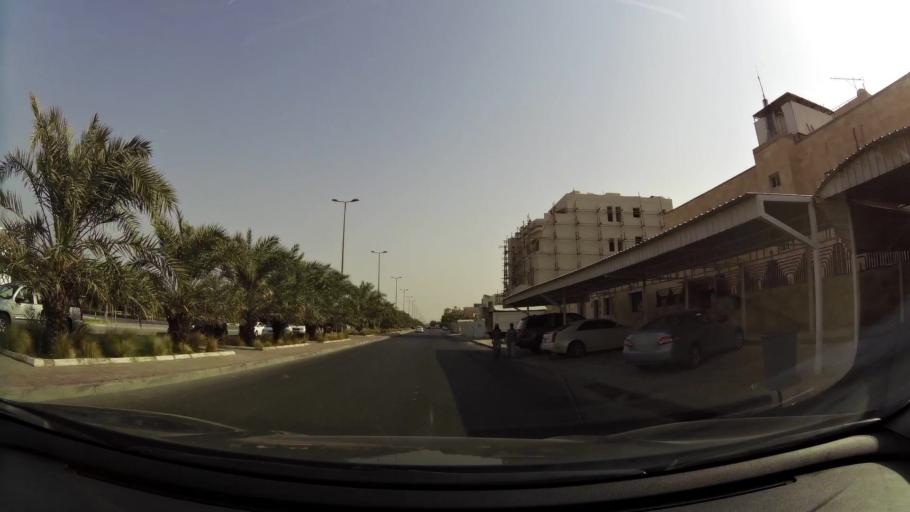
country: KW
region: Muhafazat al Jahra'
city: Al Jahra'
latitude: 29.3587
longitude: 47.6735
